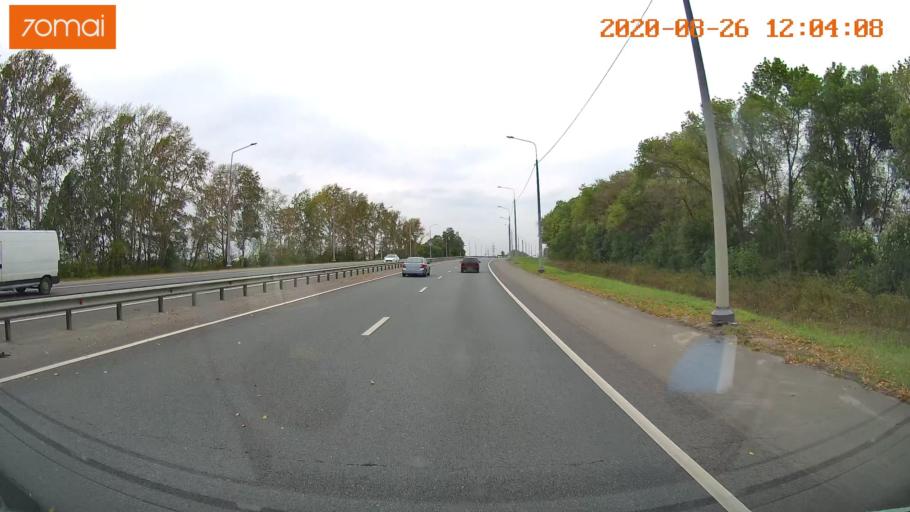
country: RU
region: Rjazan
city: Kiritsy
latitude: 54.3068
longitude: 40.1941
